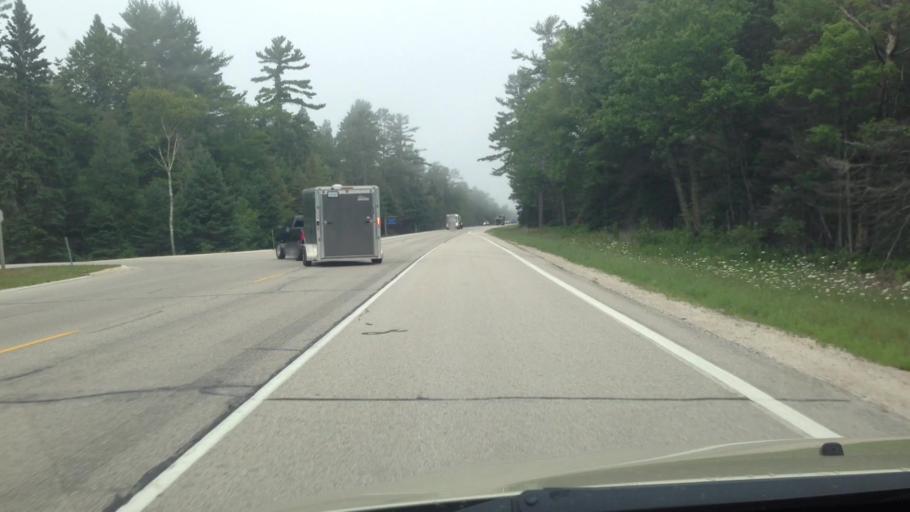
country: US
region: Michigan
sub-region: Luce County
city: Newberry
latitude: 46.0952
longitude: -85.3883
